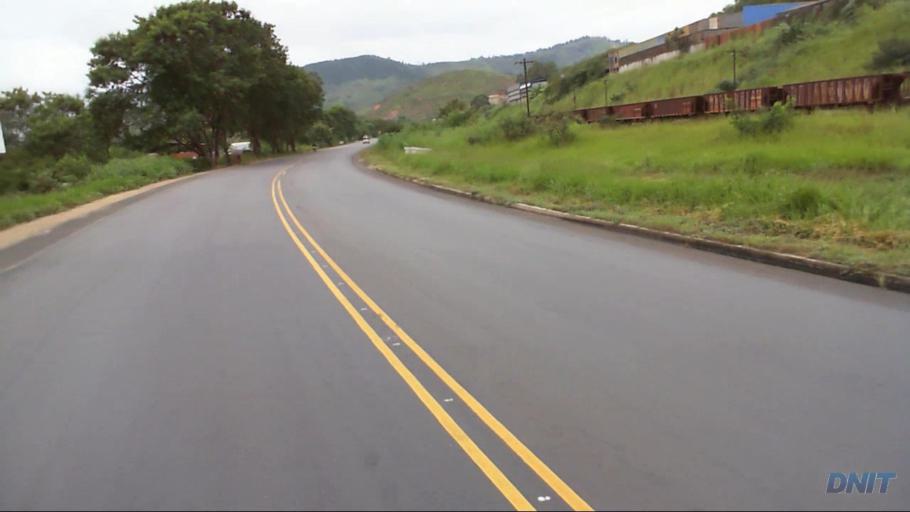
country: BR
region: Minas Gerais
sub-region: Coronel Fabriciano
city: Coronel Fabriciano
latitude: -19.5275
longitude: -42.6343
